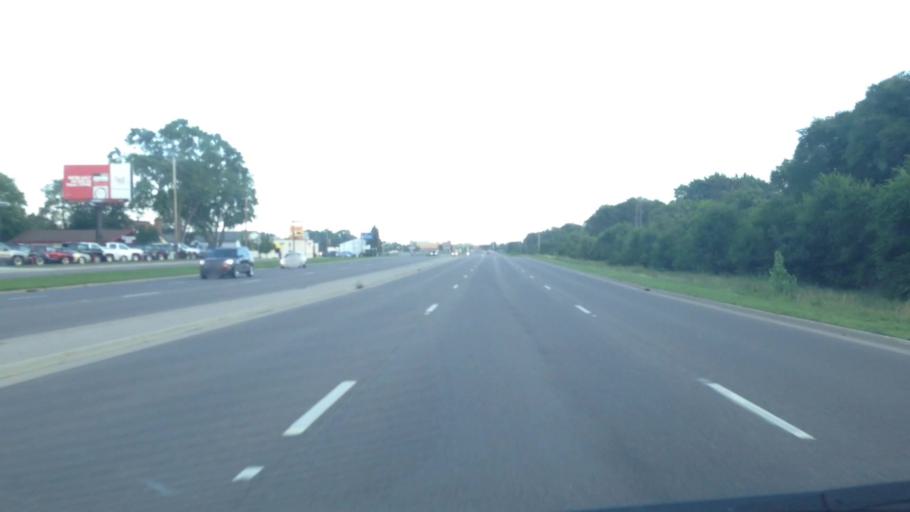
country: US
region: Minnesota
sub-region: Hennepin County
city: Brooklyn Park
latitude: 45.0643
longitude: -93.3649
